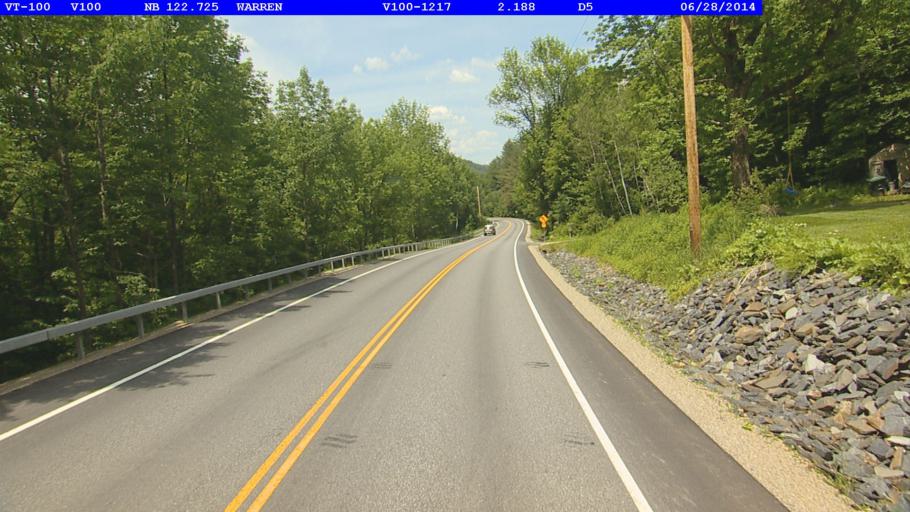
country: US
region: Vermont
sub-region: Washington County
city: Northfield
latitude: 44.0904
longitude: -72.8629
